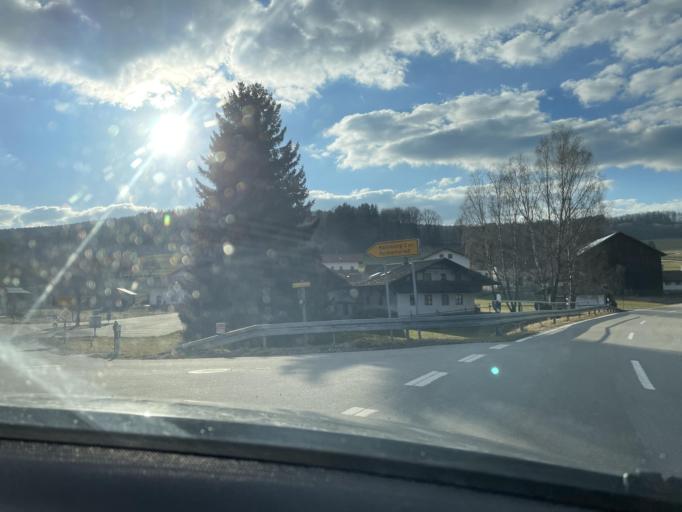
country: DE
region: Bavaria
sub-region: Lower Bavaria
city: Kollnburg
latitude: 49.0599
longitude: 12.8546
